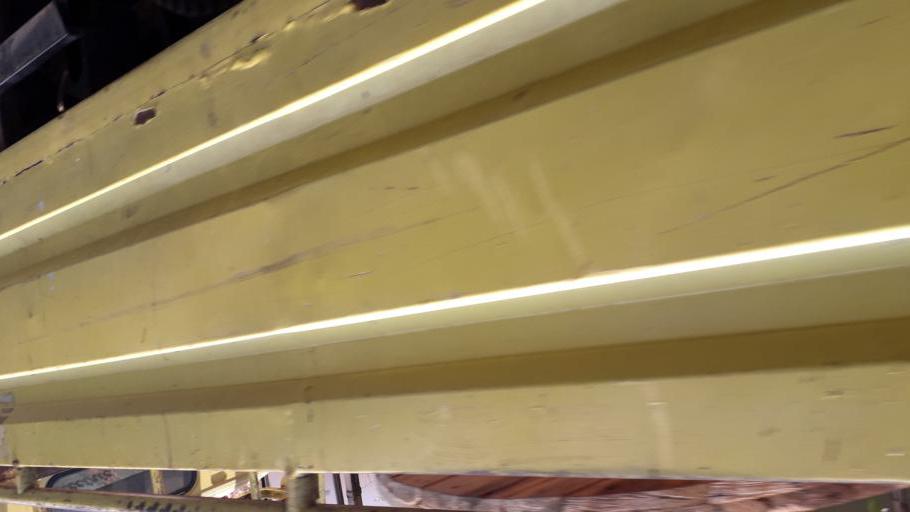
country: ID
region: Daerah Istimewa Yogyakarta
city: Yogyakarta
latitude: -7.7838
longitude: 110.3608
